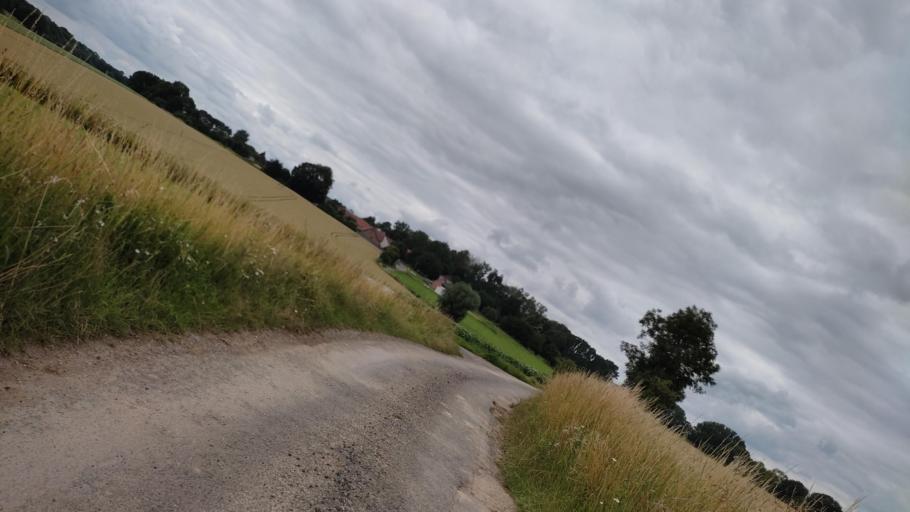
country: FR
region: Nord-Pas-de-Calais
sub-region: Departement du Pas-de-Calais
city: Beaumetz-les-Loges
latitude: 50.2595
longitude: 2.6551
